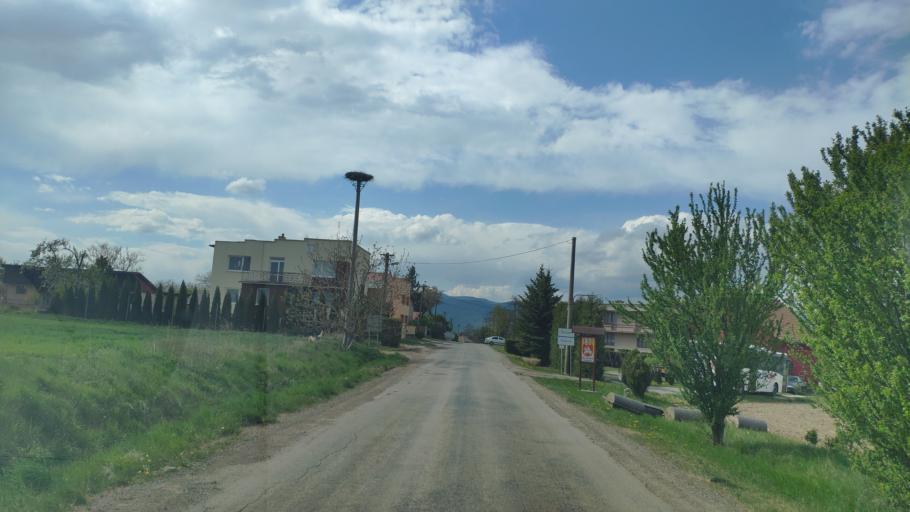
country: SK
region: Kosicky
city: Moldava nad Bodvou
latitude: 48.5803
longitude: 20.9279
